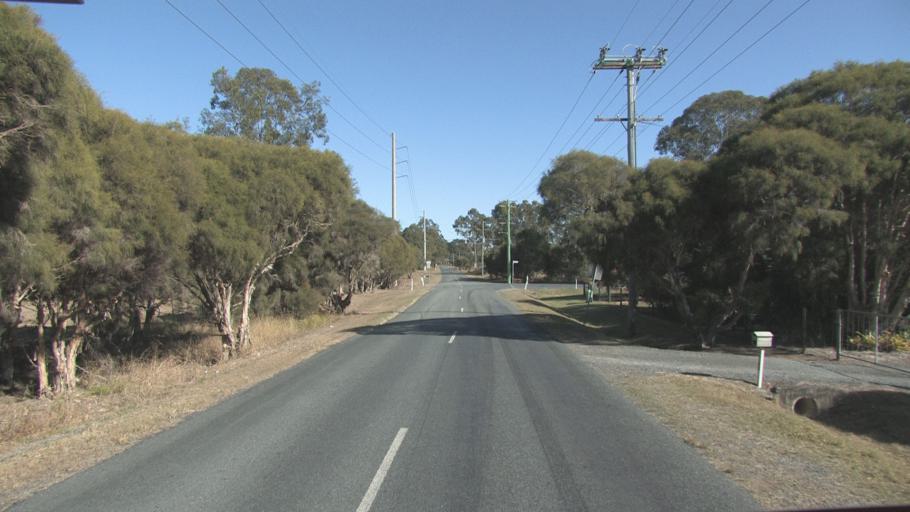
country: AU
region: Queensland
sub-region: Logan
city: Cedar Vale
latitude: -27.8408
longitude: 153.0317
